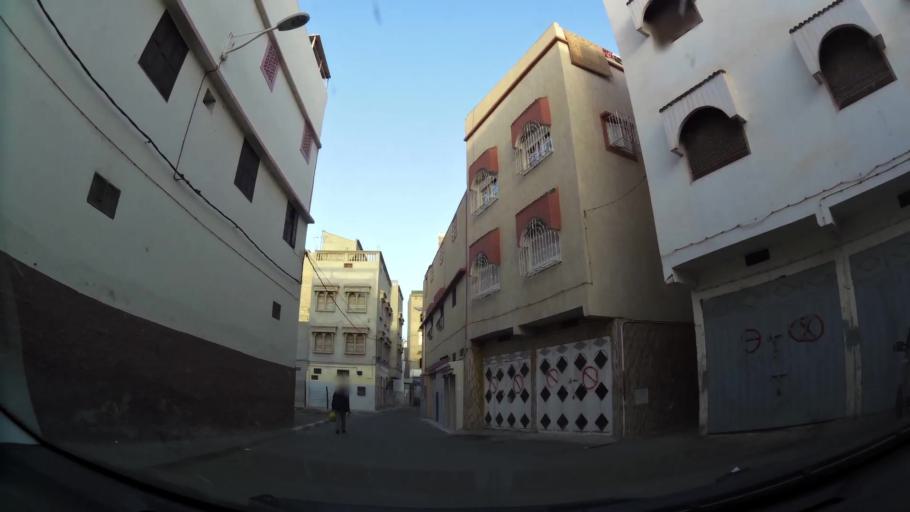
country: MA
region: Oued ed Dahab-Lagouira
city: Dakhla
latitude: 30.3887
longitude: -9.5693
